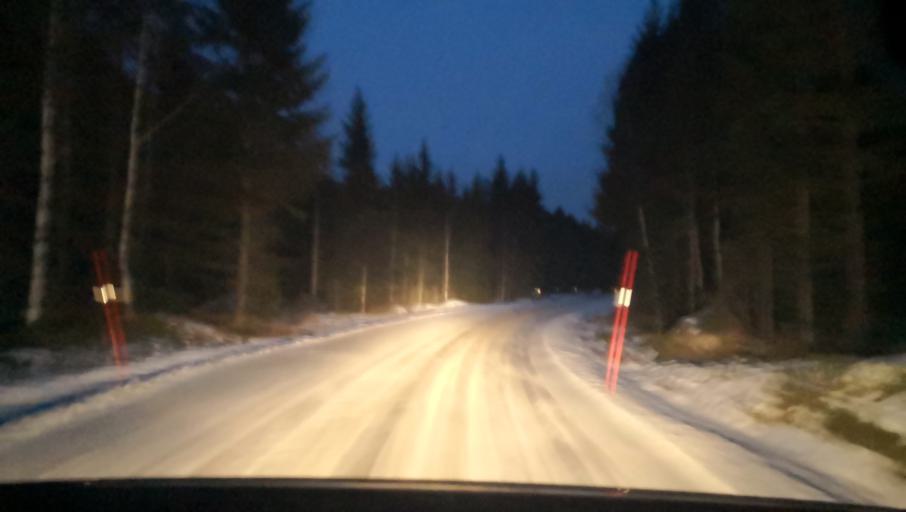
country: SE
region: Uppsala
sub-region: Heby Kommun
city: Tarnsjo
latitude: 60.2519
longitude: 16.7339
